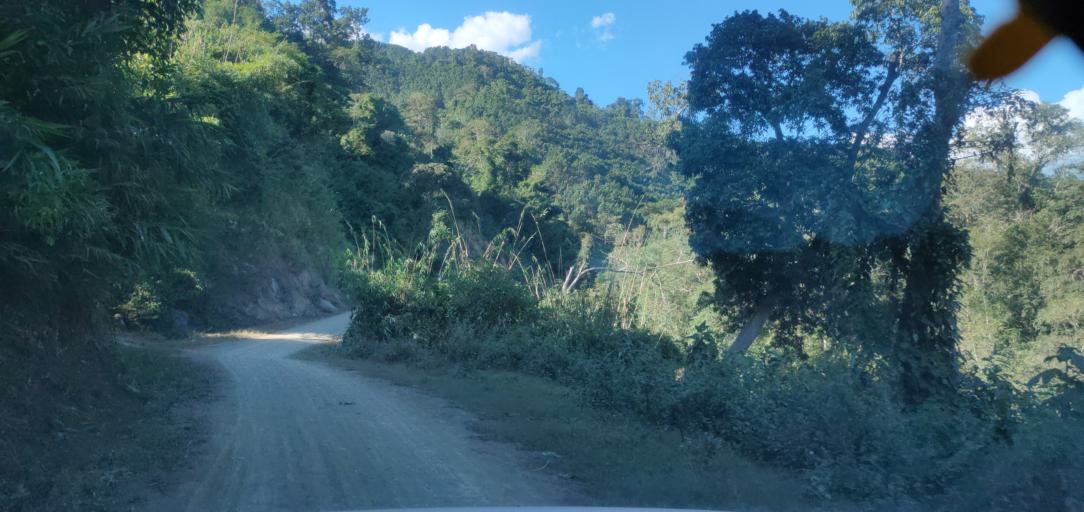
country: LA
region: Phongsali
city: Phongsali
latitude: 21.4983
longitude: 102.0903
